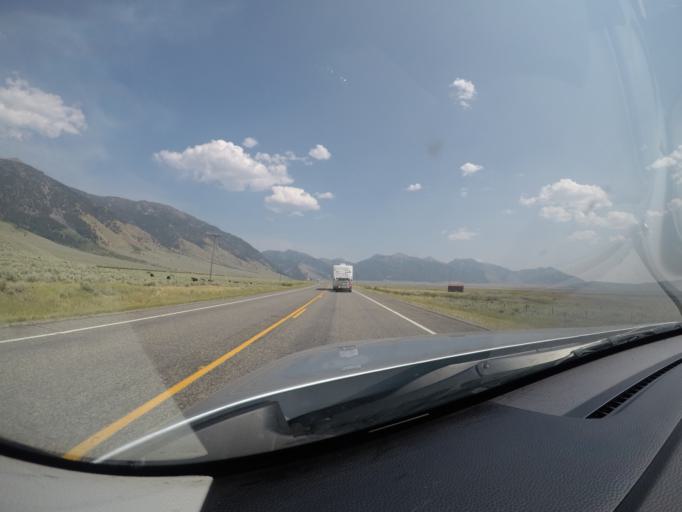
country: US
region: Montana
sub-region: Gallatin County
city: West Yellowstone
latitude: 44.8384
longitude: -111.5111
